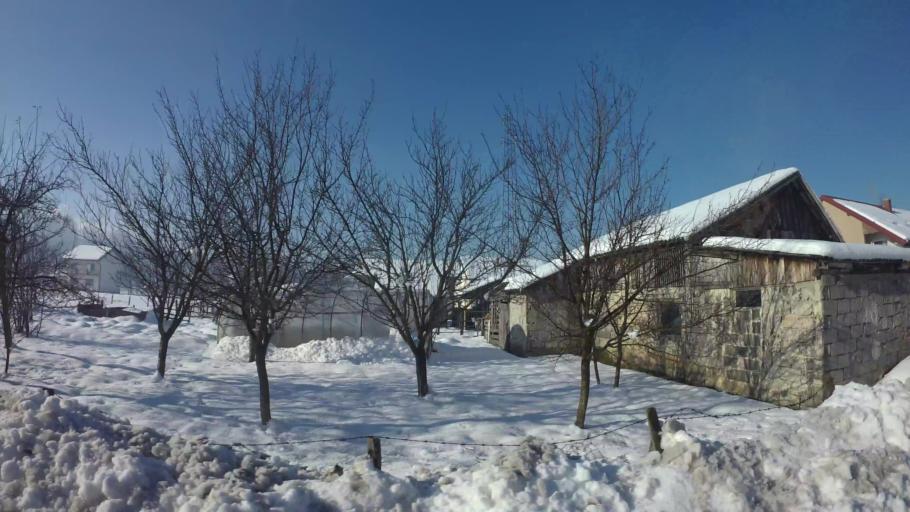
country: BA
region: Federation of Bosnia and Herzegovina
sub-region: Kanton Sarajevo
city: Sarajevo
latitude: 43.8207
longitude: 18.3786
